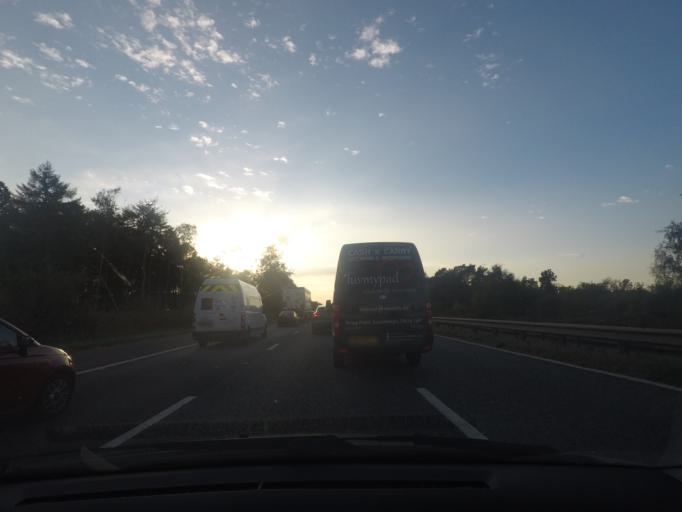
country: GB
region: England
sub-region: North Lincolnshire
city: Worlaby
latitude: 53.5813
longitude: -0.4390
